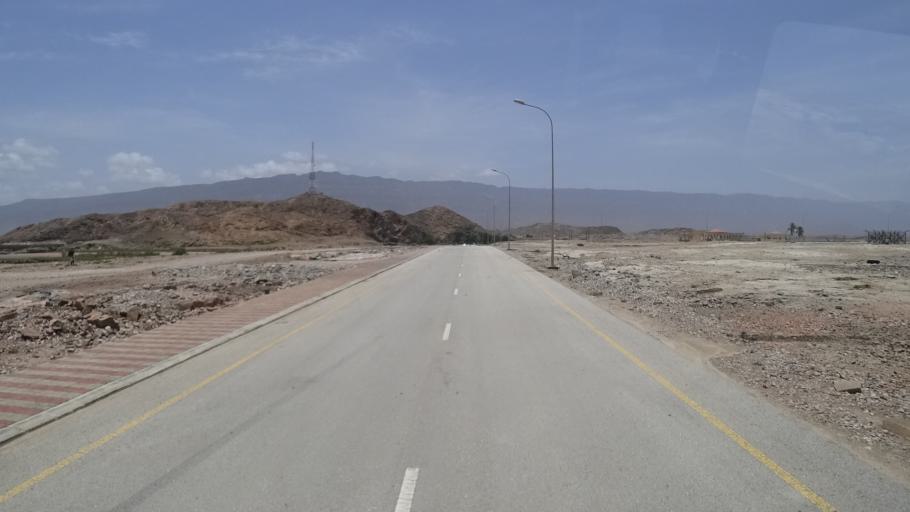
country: OM
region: Zufar
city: Salalah
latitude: 16.9956
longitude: 54.6916
